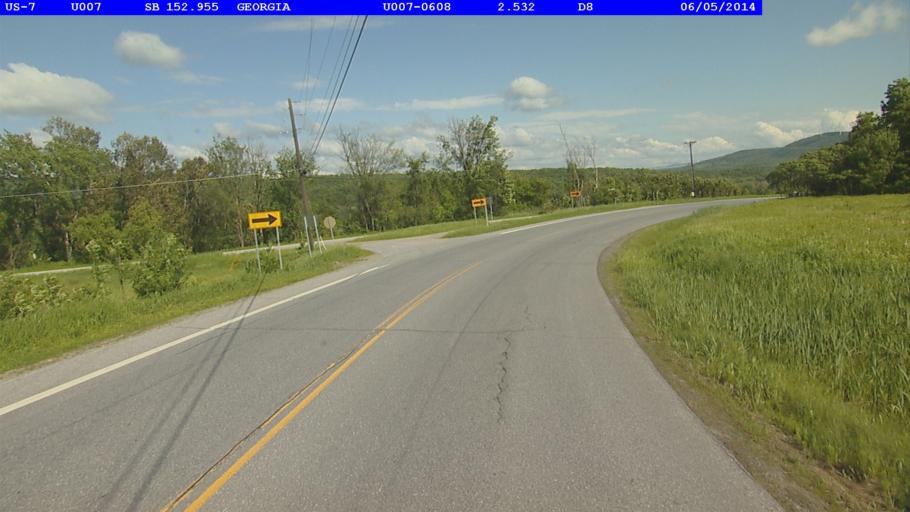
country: US
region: Vermont
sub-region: Chittenden County
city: Milton
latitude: 44.7148
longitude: -73.1020
